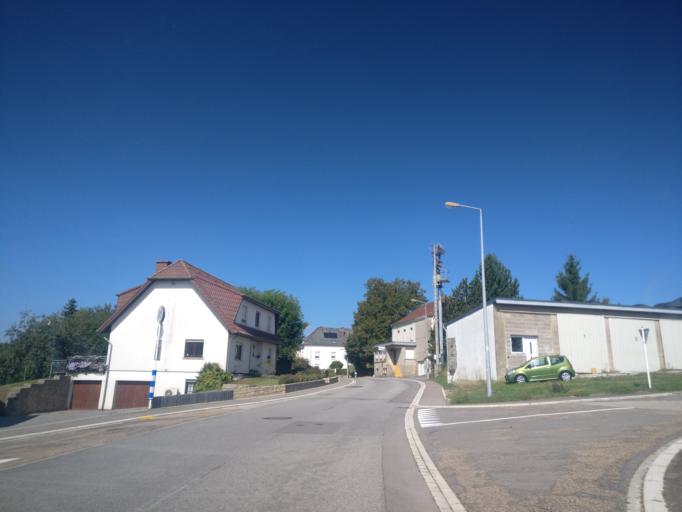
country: DE
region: Rheinland-Pfalz
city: Wellen
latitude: 49.6484
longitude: 6.3997
